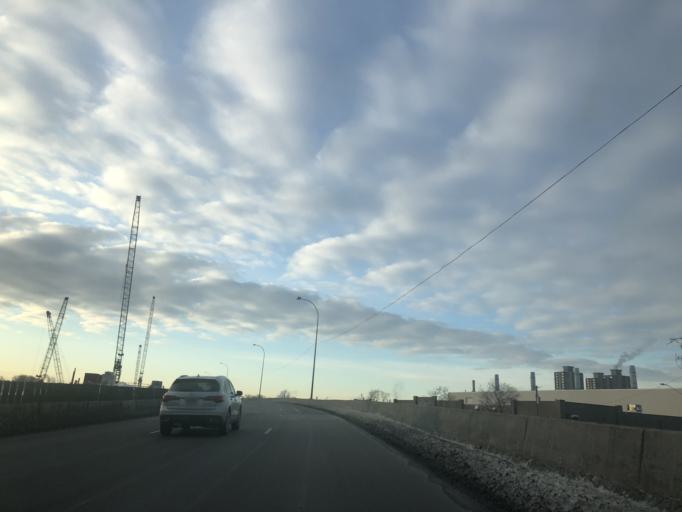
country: US
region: Minnesota
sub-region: Hennepin County
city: Minneapolis
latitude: 44.9511
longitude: -93.2756
